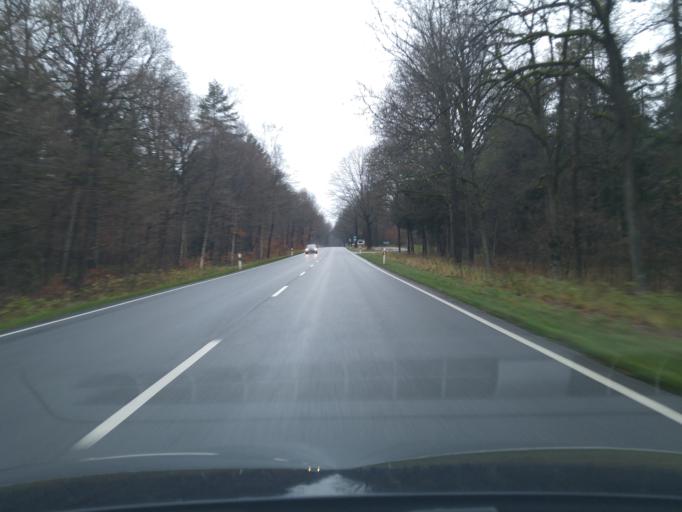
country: DE
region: Lower Saxony
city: Sprakensehl
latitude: 52.8054
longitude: 10.4877
